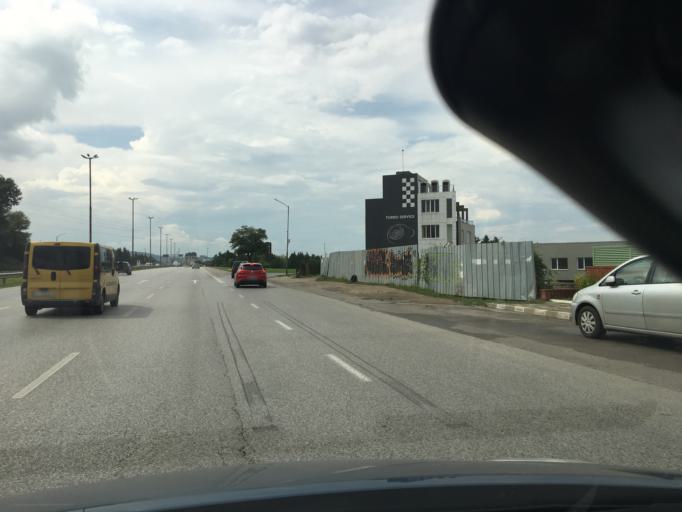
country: BG
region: Sofia-Capital
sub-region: Stolichna Obshtina
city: Sofia
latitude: 42.6519
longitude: 23.2877
